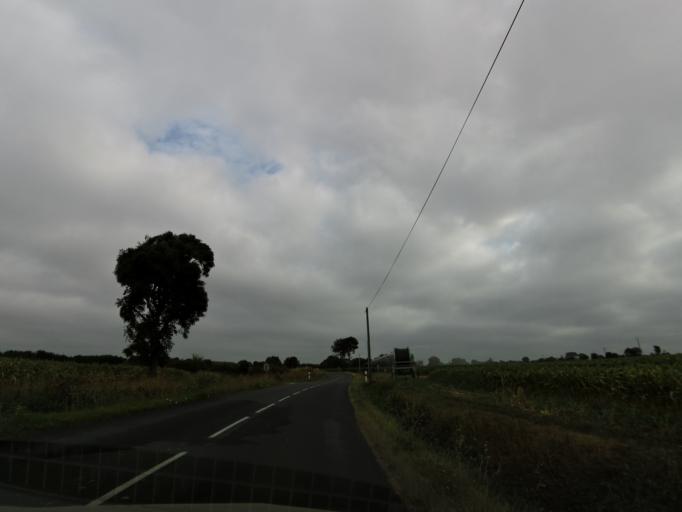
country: FR
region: Pays de la Loire
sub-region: Departement de la Vendee
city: Avrille
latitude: 46.4537
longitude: -1.4596
